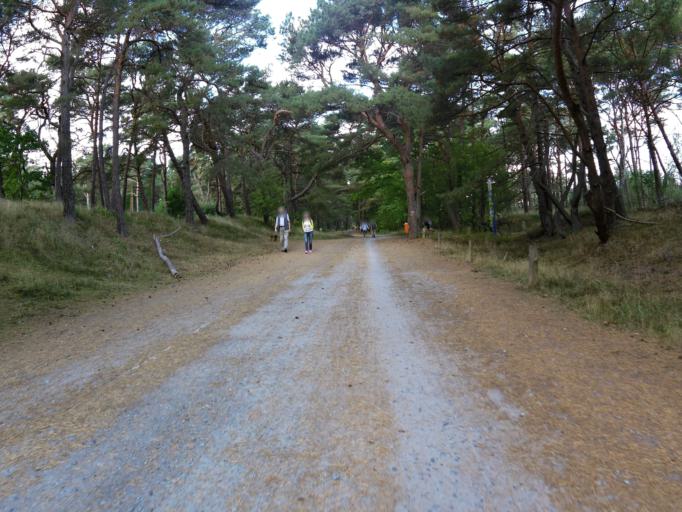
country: DE
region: Mecklenburg-Vorpommern
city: Ostseebad Zinnowitz
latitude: 54.0918
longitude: 13.8884
